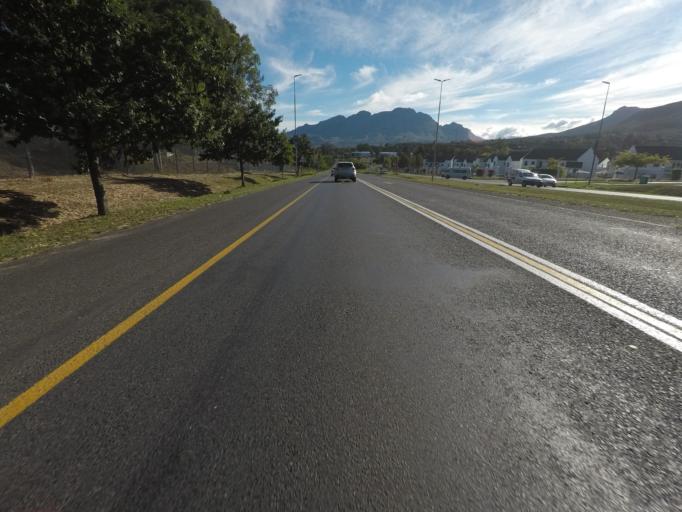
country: ZA
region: Western Cape
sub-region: Cape Winelands District Municipality
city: Stellenbosch
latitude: -33.9598
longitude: 18.8527
